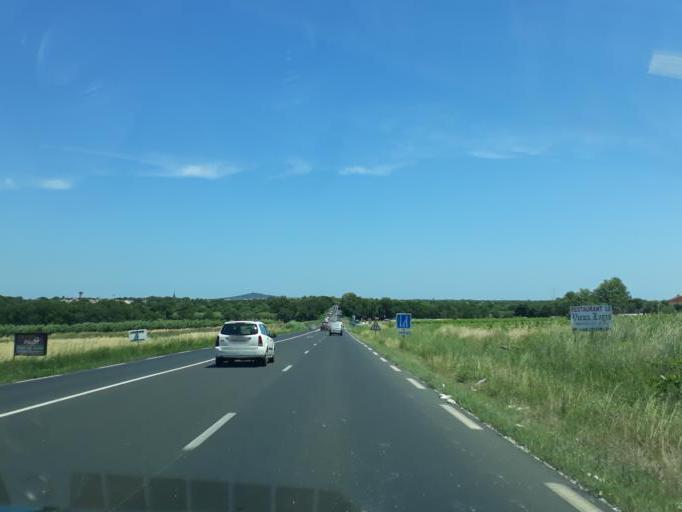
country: FR
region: Languedoc-Roussillon
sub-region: Departement de l'Herault
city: Vias
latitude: 43.3143
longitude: 3.3851
